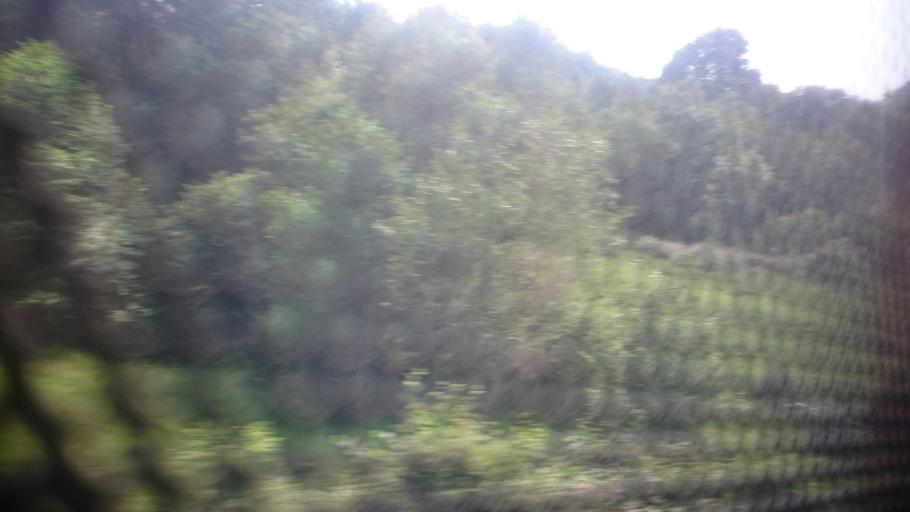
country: ES
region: Asturias
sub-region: Province of Asturias
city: Amieva
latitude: 43.2995
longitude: -5.0331
